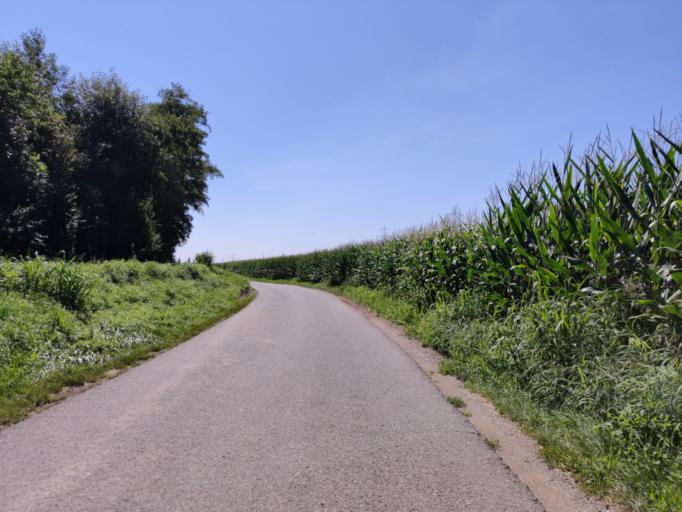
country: AT
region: Styria
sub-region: Politischer Bezirk Leibnitz
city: Ragnitz
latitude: 46.8321
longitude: 15.5583
